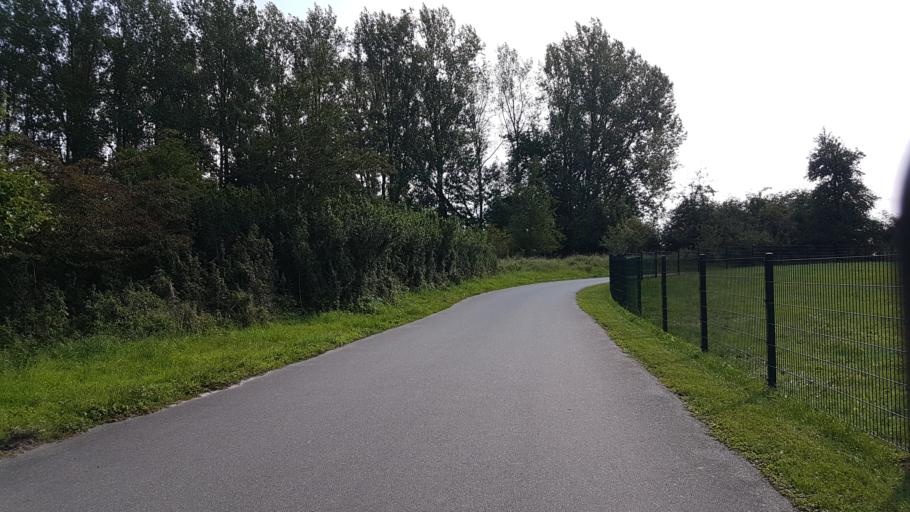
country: DE
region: Mecklenburg-Vorpommern
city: Glowe
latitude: 54.5606
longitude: 13.4854
